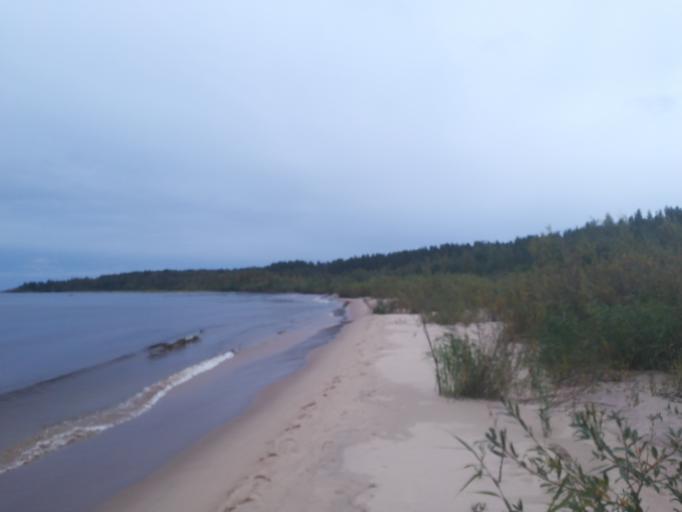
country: RU
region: Leningrad
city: Priozersk
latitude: 61.0403
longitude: 30.1926
